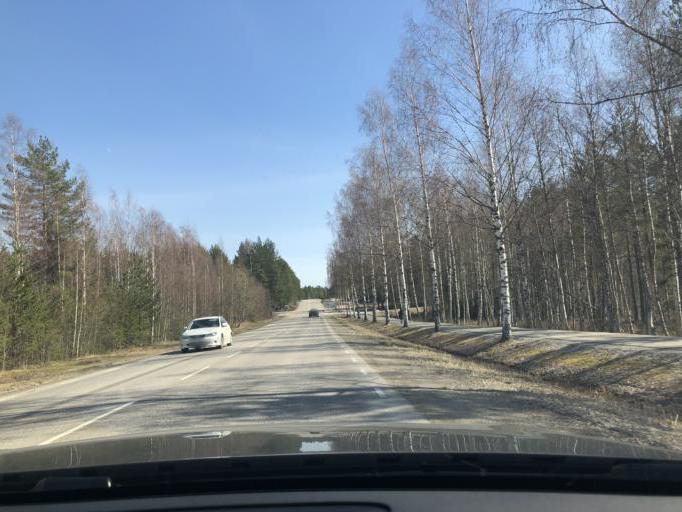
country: SE
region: Gaevleborg
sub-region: Hudiksvalls Kommun
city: Hudiksvall
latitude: 61.7248
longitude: 17.1568
